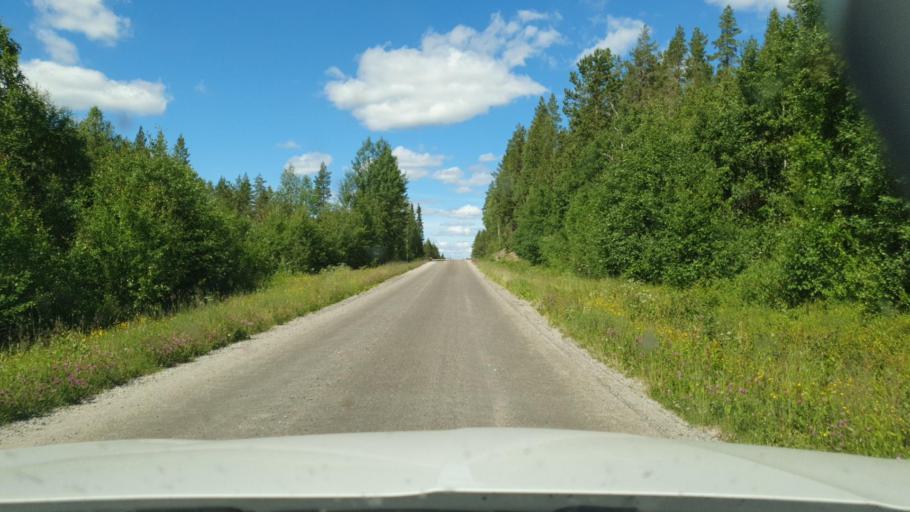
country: SE
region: Vaesterbotten
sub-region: Skelleftea Kommun
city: Backa
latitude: 65.1440
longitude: 21.1724
